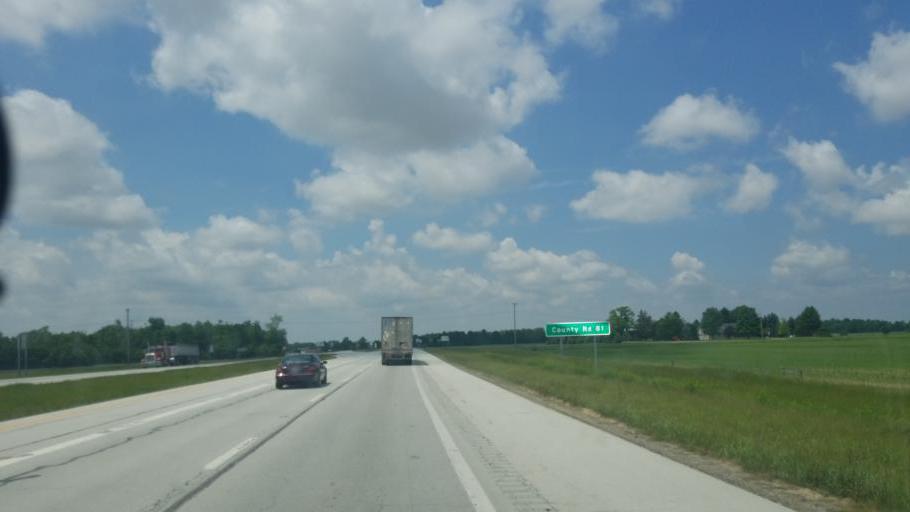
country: US
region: Ohio
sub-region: Hardin County
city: Forest
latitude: 40.8259
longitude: -83.4746
